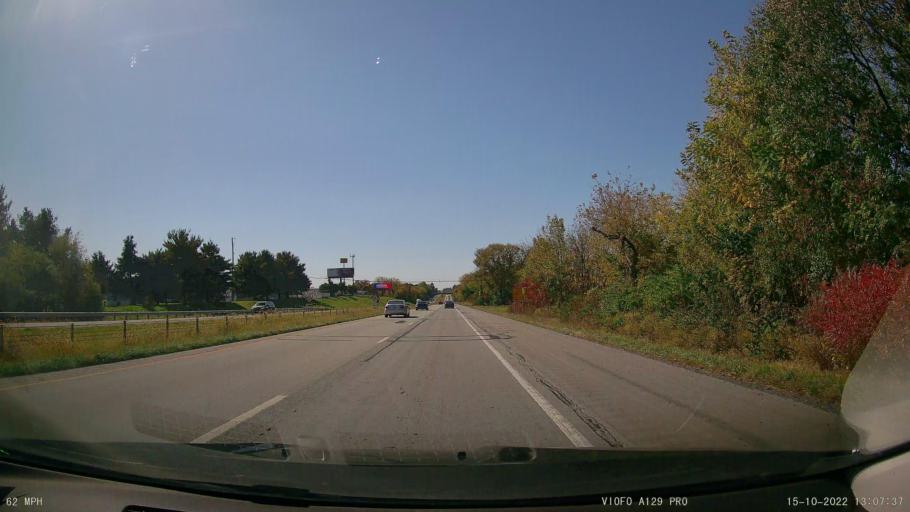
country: US
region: Pennsylvania
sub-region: Berks County
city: River View Park
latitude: 40.4054
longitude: -75.9500
